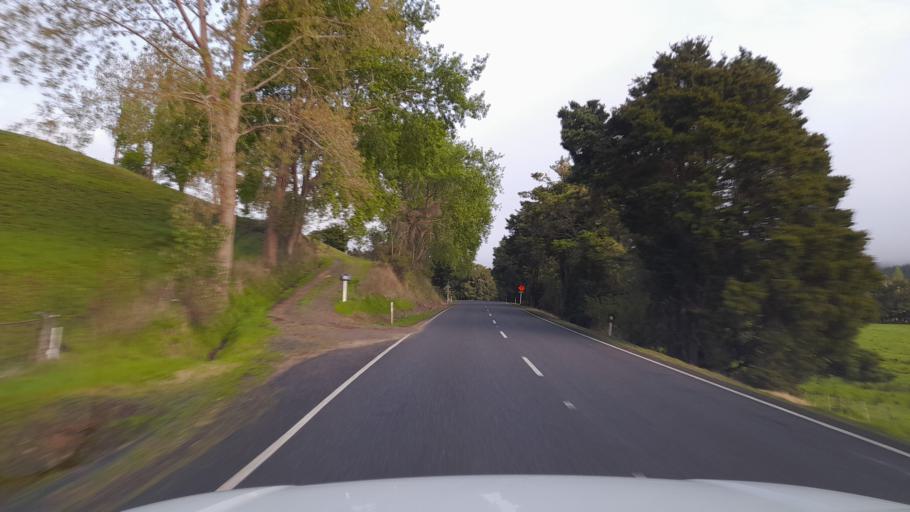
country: NZ
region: Northland
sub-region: Kaipara District
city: Dargaville
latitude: -35.6477
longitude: 173.8650
